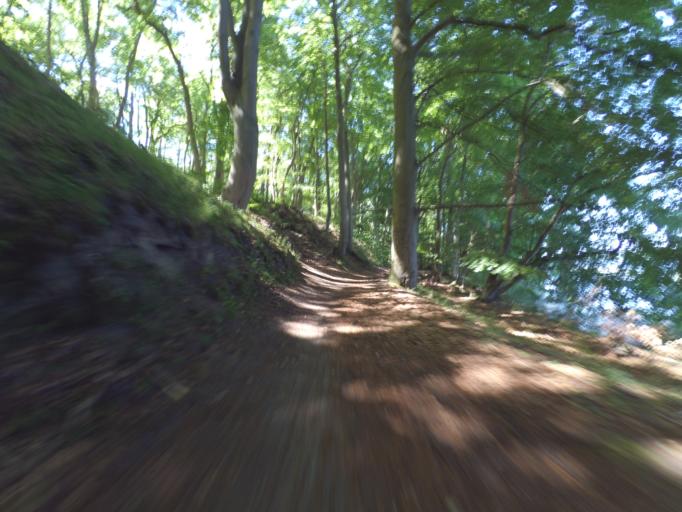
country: DE
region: Mecklenburg-Vorpommern
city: Malchow
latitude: 53.4762
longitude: 12.3570
